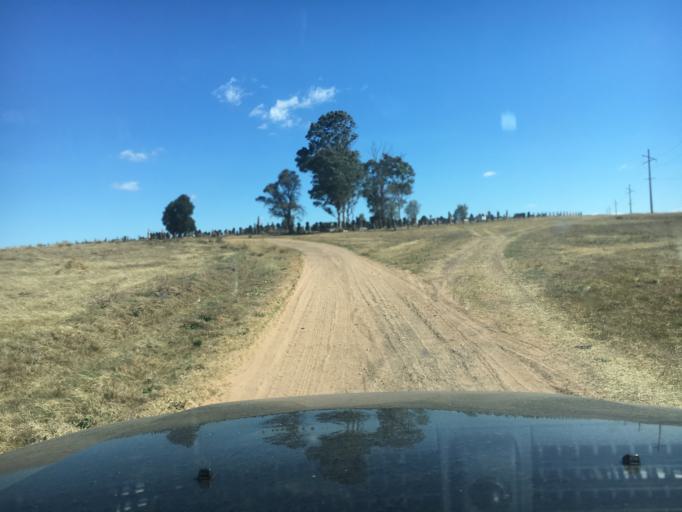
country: AU
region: New South Wales
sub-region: Singleton
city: Singleton
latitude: -32.5892
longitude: 151.1829
